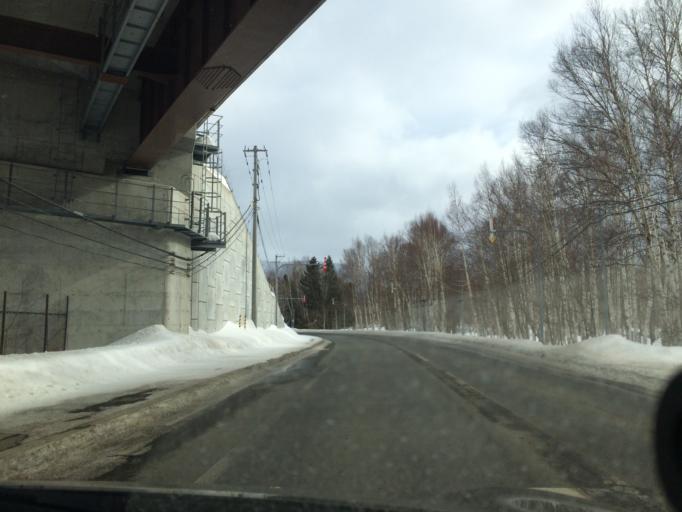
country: JP
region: Hokkaido
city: Shimo-furano
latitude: 43.0527
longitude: 142.6438
